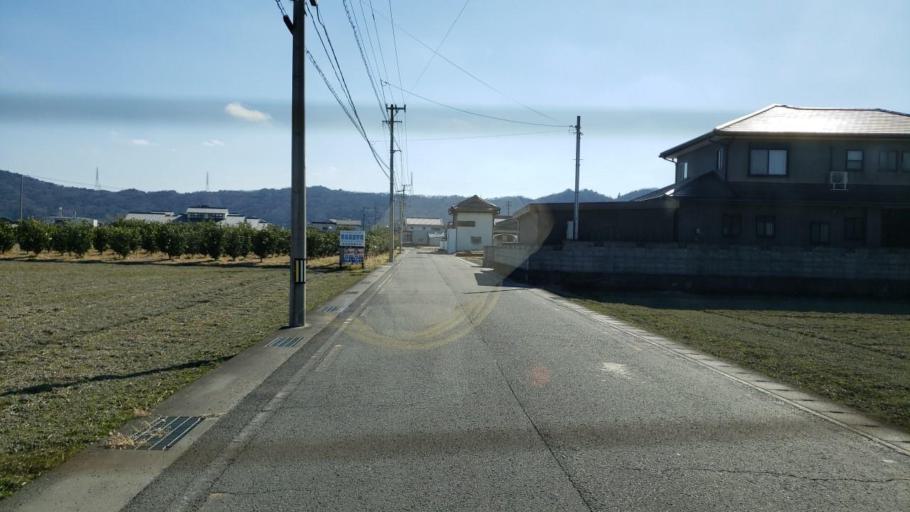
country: JP
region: Tokushima
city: Ishii
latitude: 34.0718
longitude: 134.4335
